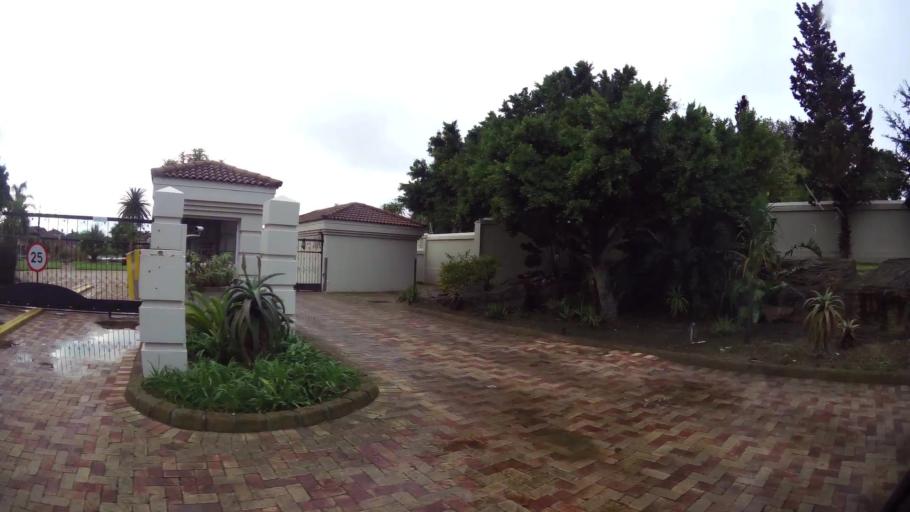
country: ZA
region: Eastern Cape
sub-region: Nelson Mandela Bay Metropolitan Municipality
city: Port Elizabeth
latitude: -33.9948
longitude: 25.5628
